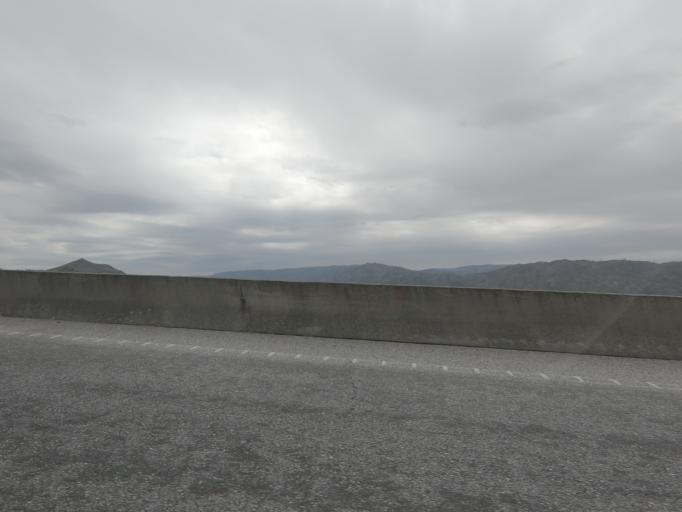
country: PT
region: Guarda
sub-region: Guarda
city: Guarda
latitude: 40.5954
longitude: -7.2758
